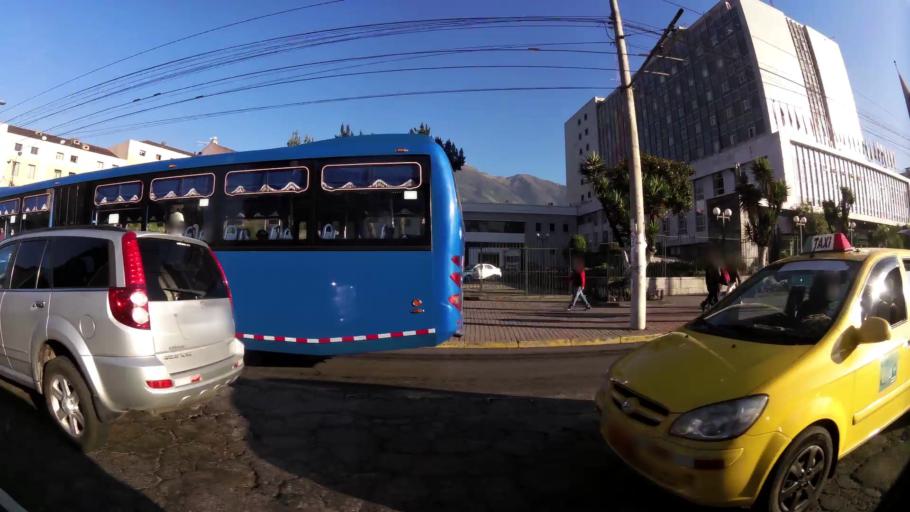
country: EC
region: Pichincha
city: Quito
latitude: -0.2162
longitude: -78.5048
